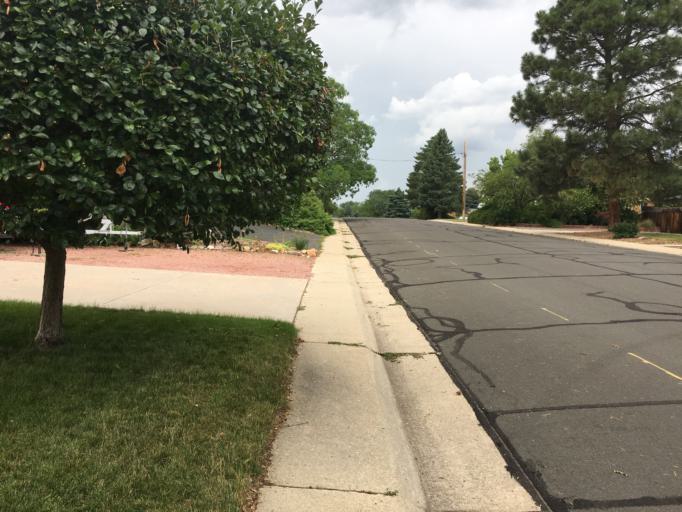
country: US
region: Colorado
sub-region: Arapahoe County
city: Glendale
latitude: 39.6724
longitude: -104.9237
